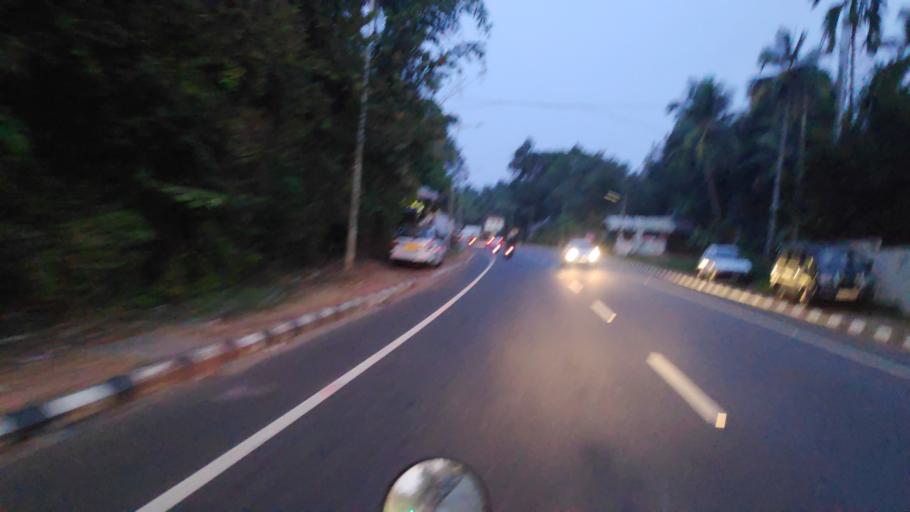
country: IN
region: Kerala
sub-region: Kozhikode
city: Kunnamangalam
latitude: 11.2811
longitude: 75.8272
